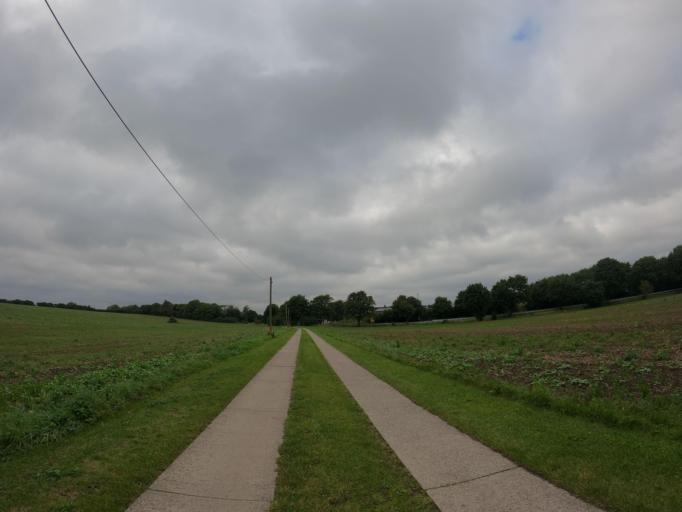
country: DE
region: Mecklenburg-Vorpommern
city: Altefahr
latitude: 54.3219
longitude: 13.1448
